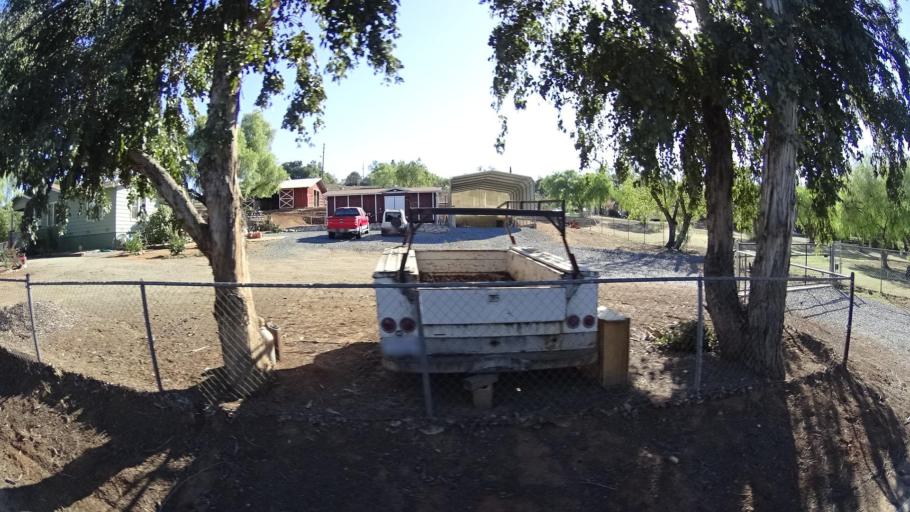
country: US
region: California
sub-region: San Diego County
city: Jamul
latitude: 32.7114
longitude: -116.8808
